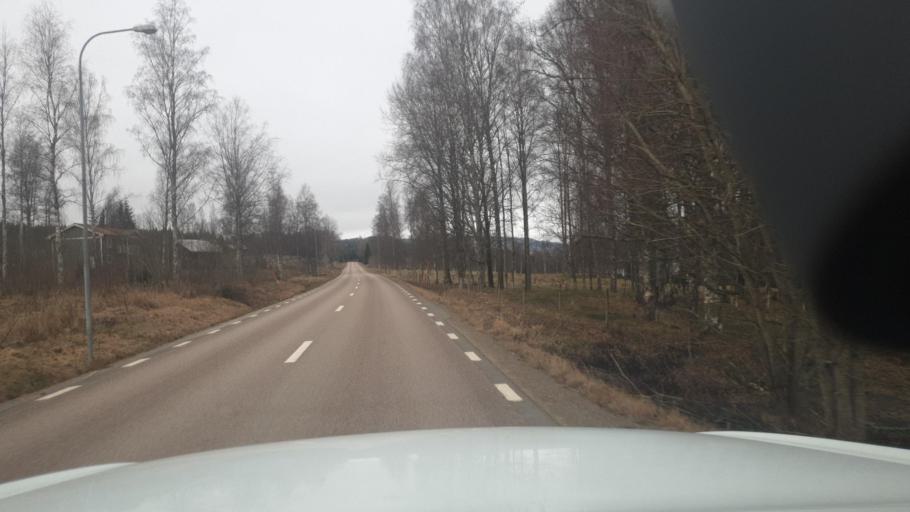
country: SE
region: Vaermland
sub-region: Sunne Kommun
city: Sunne
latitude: 59.8982
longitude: 12.9150
